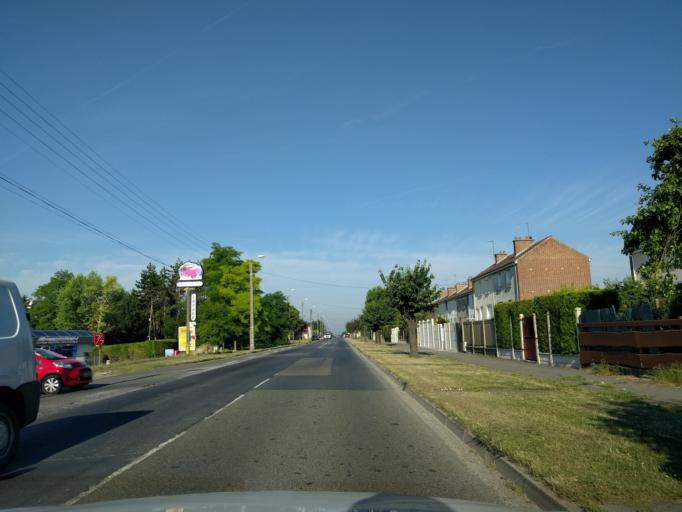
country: FR
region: Picardie
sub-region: Departement de la Somme
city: Montdidier
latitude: 49.6474
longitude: 2.5875
